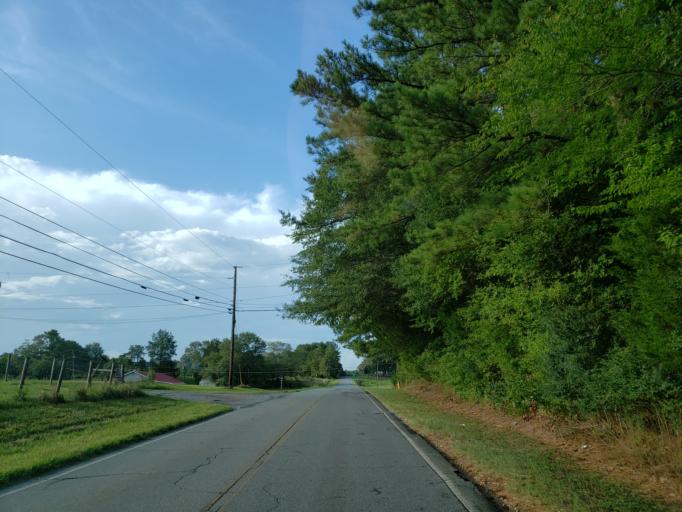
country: US
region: Georgia
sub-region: Bartow County
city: Euharlee
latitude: 34.2196
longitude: -84.9687
